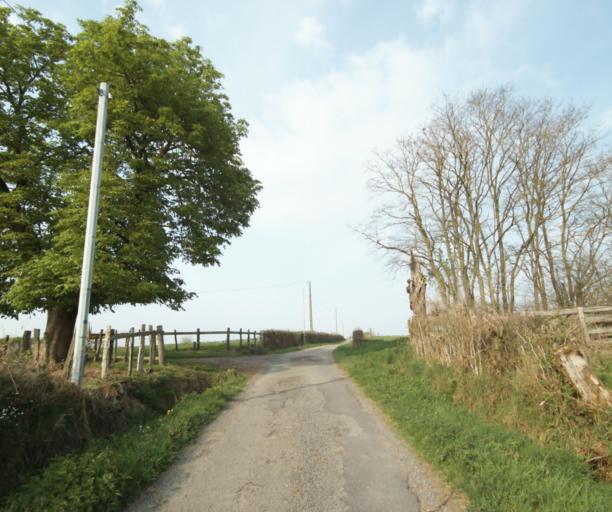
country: FR
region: Bourgogne
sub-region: Departement de Saone-et-Loire
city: Matour
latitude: 46.4634
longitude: 4.4490
